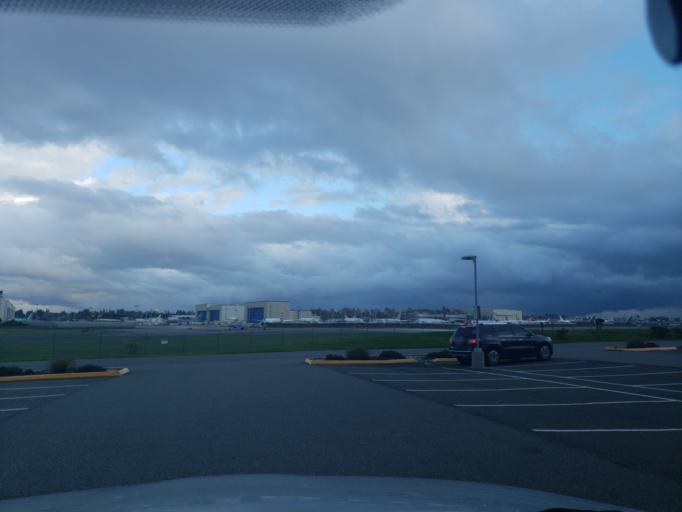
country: US
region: Washington
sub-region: Snohomish County
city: Mukilteo
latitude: 47.9228
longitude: -122.2889
